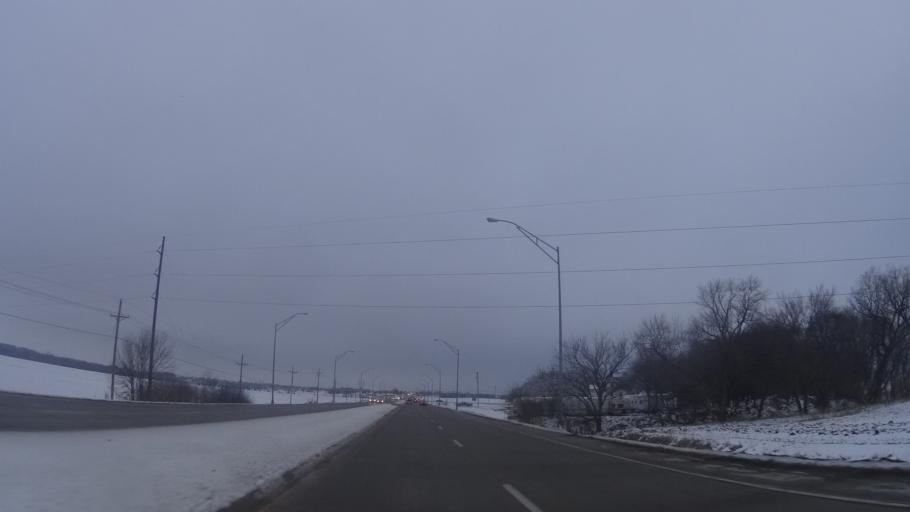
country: US
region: Nebraska
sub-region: Sarpy County
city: La Vista
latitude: 41.1619
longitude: -95.9792
